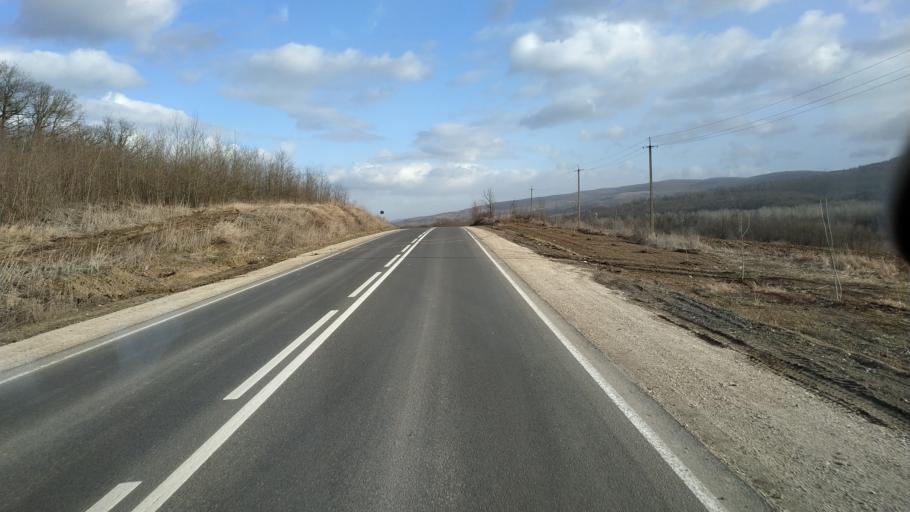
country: MD
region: Calarasi
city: Calarasi
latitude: 47.3085
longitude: 28.1278
